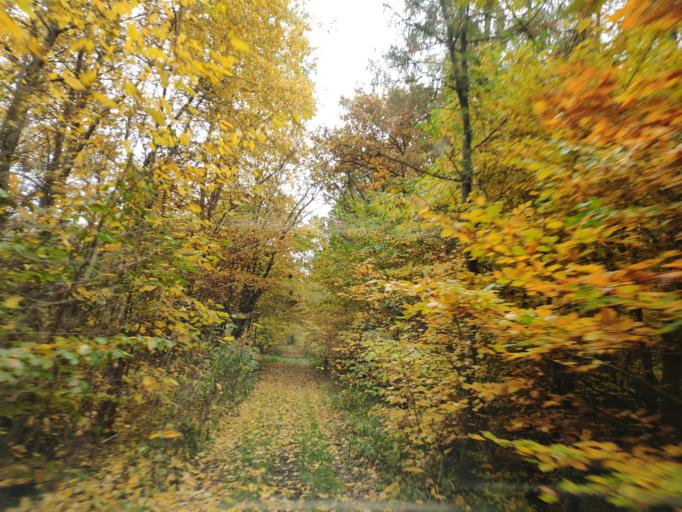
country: SK
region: Kosicky
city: Kosice
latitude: 48.7231
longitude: 21.1073
